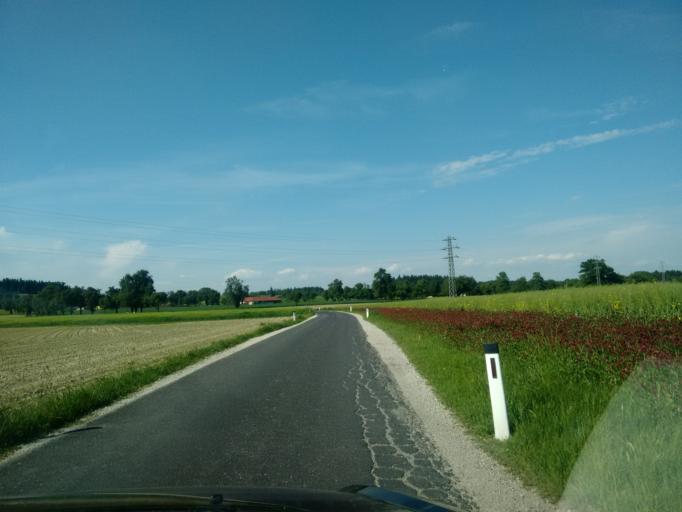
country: AT
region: Upper Austria
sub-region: Wels-Land
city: Gunskirchen
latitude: 48.1738
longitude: 13.9649
